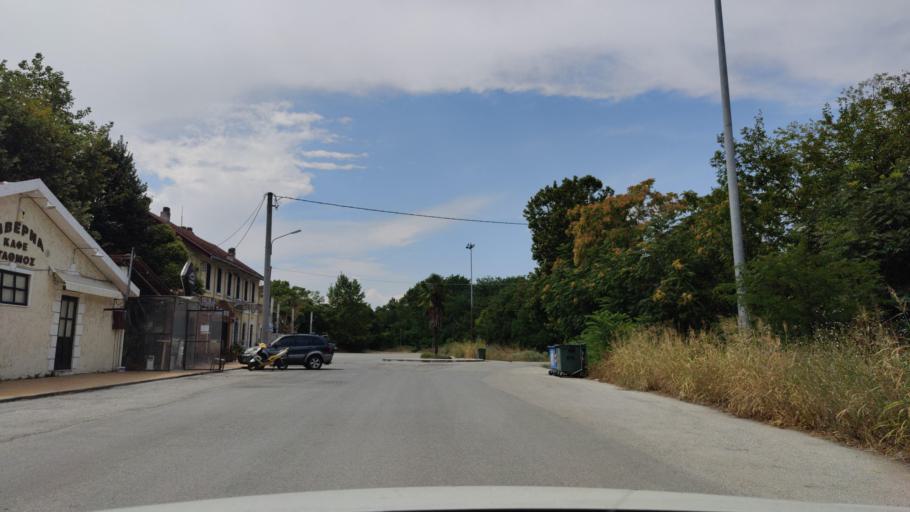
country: GR
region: Central Macedonia
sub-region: Nomos Serron
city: Serres
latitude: 41.0741
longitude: 23.5372
